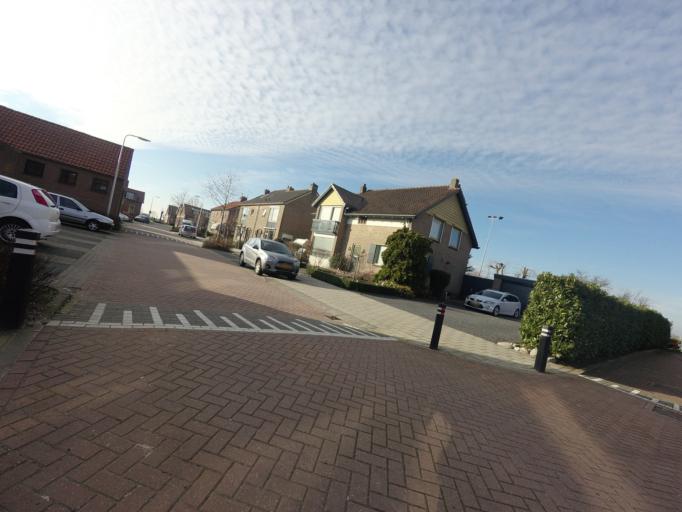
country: NL
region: South Holland
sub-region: Gemeente Vlist
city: Haastrecht
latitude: 52.0446
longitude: 4.7972
